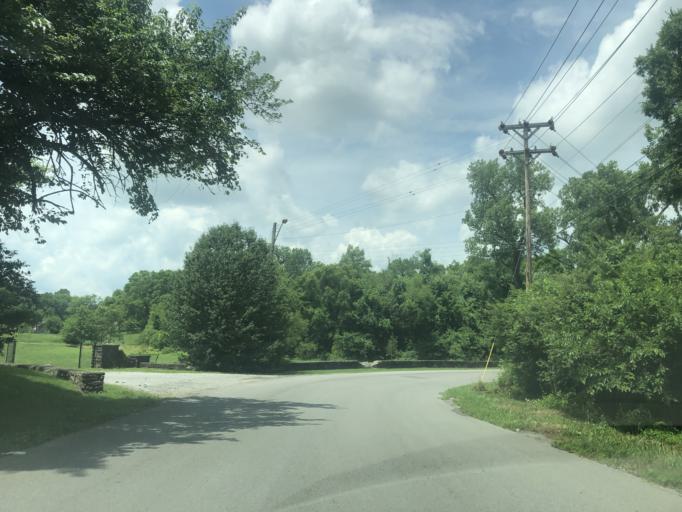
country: US
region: Tennessee
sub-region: Davidson County
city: Nashville
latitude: 36.1891
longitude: -86.8052
